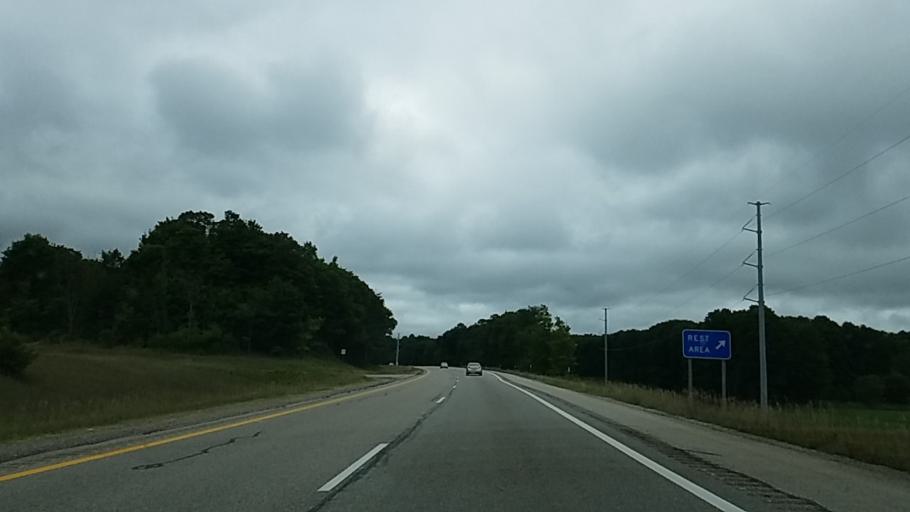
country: US
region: Michigan
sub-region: Otsego County
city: Gaylord
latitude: 45.1132
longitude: -84.6855
